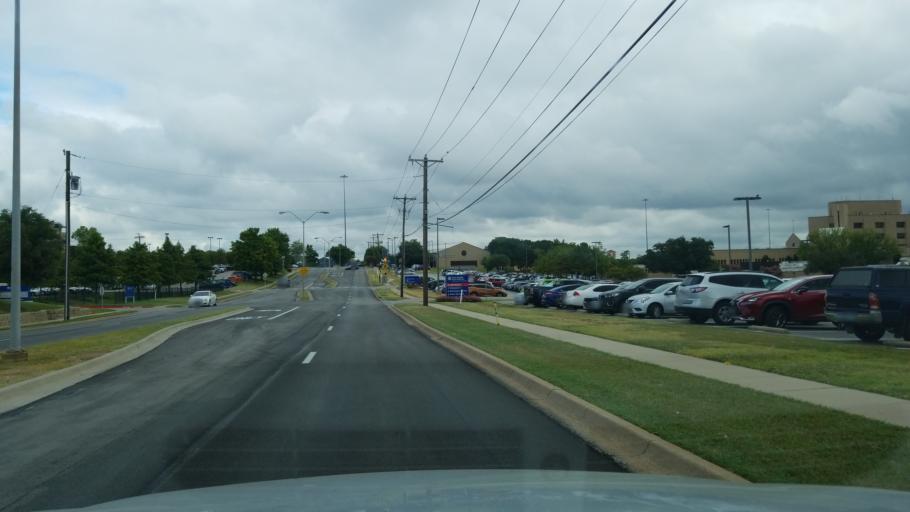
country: US
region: Texas
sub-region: Tarrant County
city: Bedford
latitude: 32.8333
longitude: -97.1252
